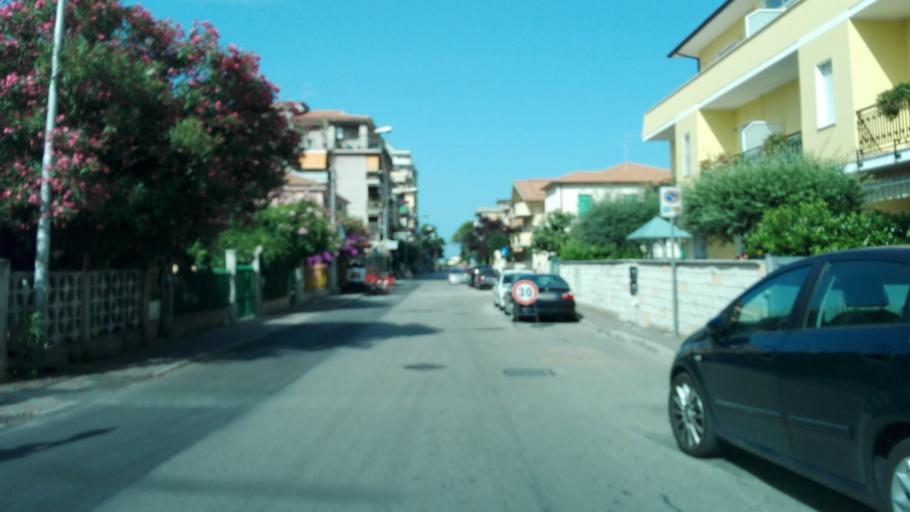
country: IT
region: Abruzzo
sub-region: Provincia di Pescara
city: Montesilvano Marina
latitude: 42.4981
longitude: 14.1760
